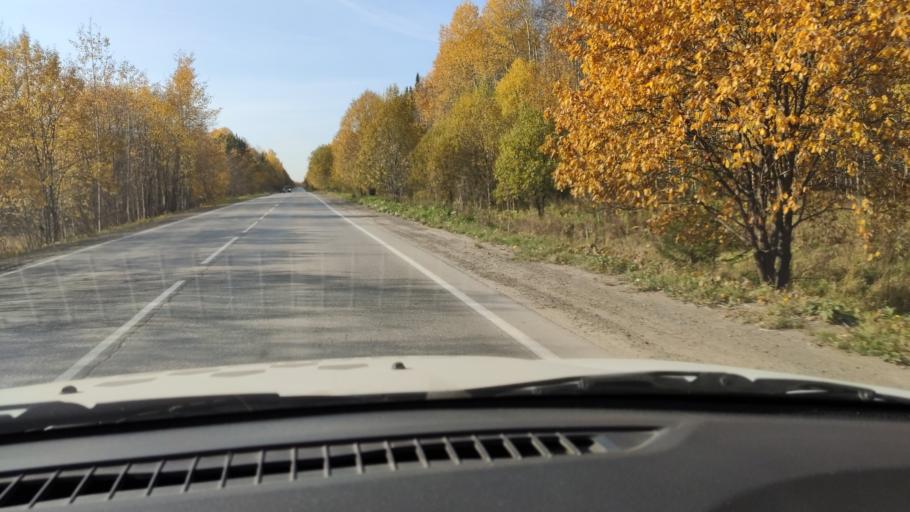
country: RU
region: Perm
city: Novyye Lyady
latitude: 58.0229
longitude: 56.6614
